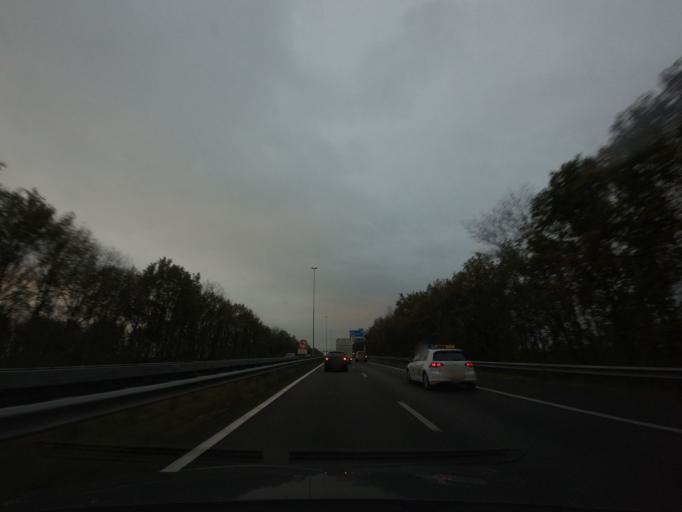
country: NL
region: North Brabant
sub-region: Gemeente Breda
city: Hoge Vucht
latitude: 51.5990
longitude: 4.8366
